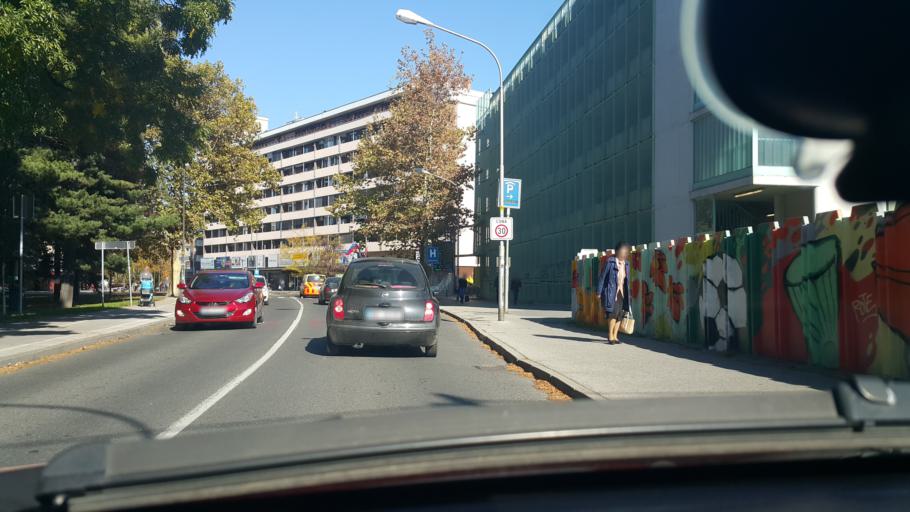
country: SI
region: Maribor
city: Maribor
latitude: 46.5519
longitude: 15.6464
